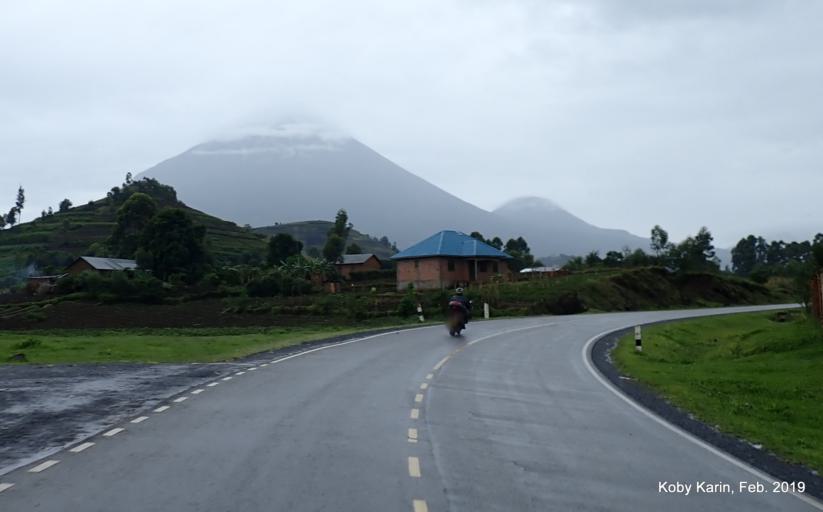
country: UG
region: Western Region
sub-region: Kisoro District
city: Kisoro
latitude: -1.3061
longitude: 29.7248
